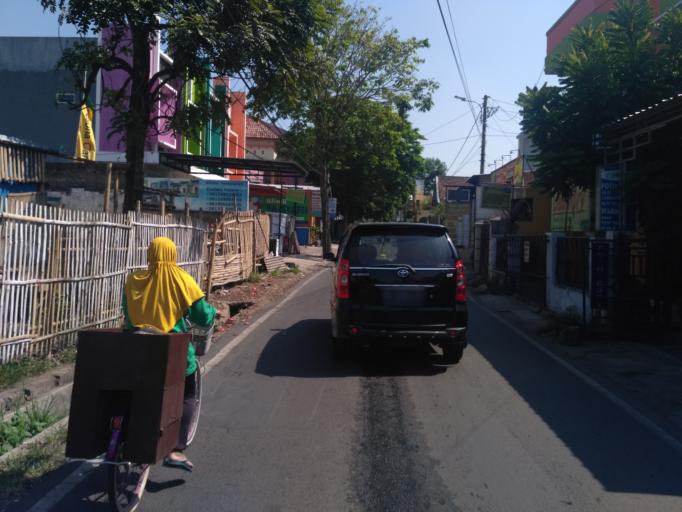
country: ID
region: East Java
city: Malang
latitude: -7.9336
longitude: 112.6140
